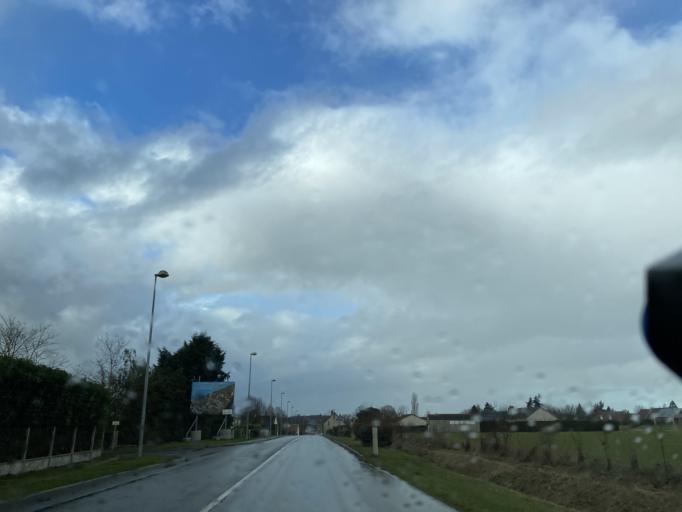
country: FR
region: Centre
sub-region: Departement d'Eure-et-Loir
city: Saint-Aubin-des-Bois
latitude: 48.5048
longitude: 1.3531
